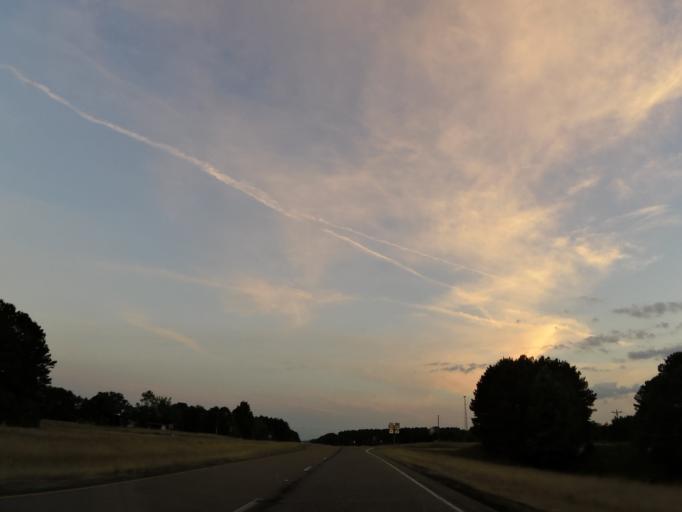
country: US
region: Mississippi
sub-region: Kemper County
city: De Kalb
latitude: 32.6875
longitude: -88.4887
